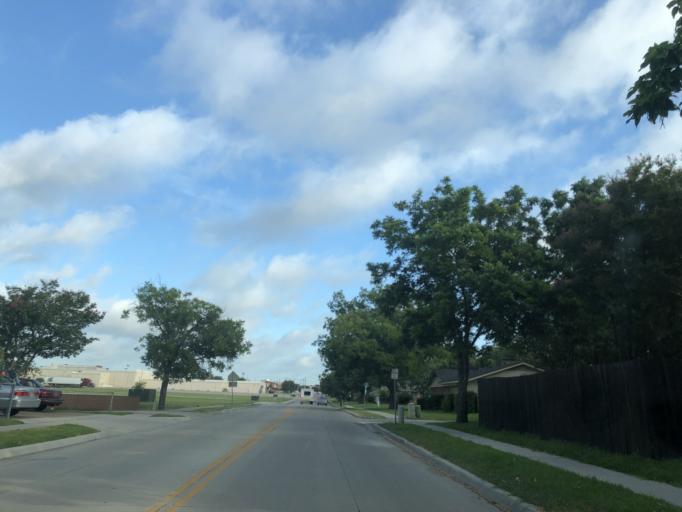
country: US
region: Texas
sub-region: Dallas County
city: Garland
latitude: 32.8557
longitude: -96.6413
